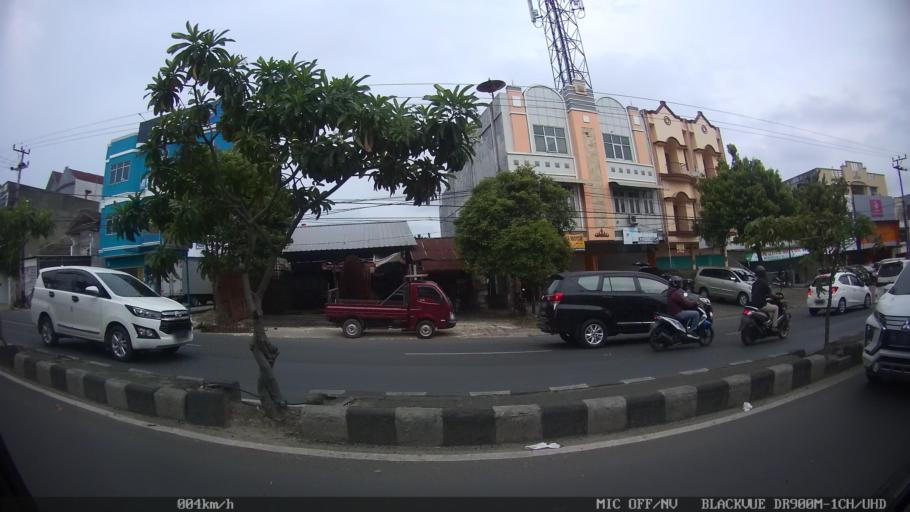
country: ID
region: Lampung
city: Bandarlampung
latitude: -5.4052
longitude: 105.2775
